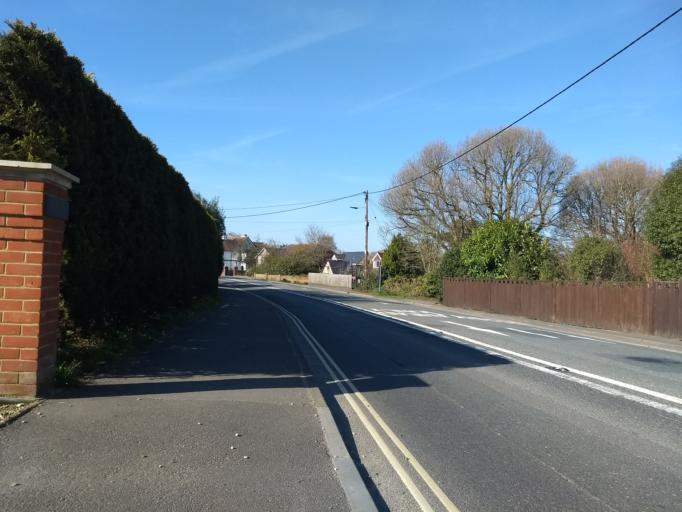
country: GB
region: England
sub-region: Isle of Wight
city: Ryde
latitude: 50.7308
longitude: -1.2148
